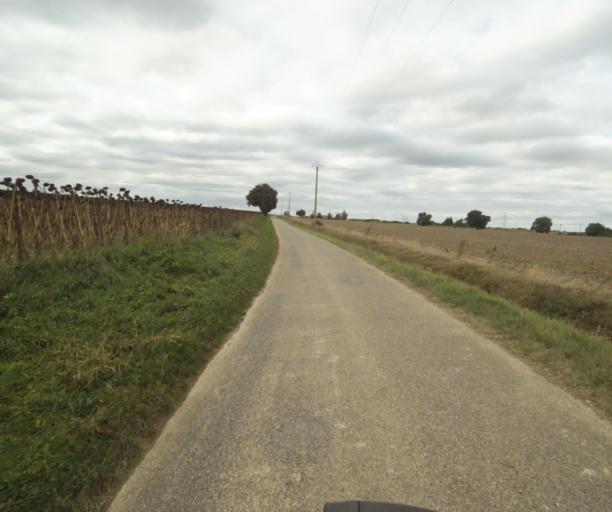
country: FR
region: Midi-Pyrenees
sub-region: Departement du Tarn-et-Garonne
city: Verdun-sur-Garonne
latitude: 43.8695
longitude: 1.1689
